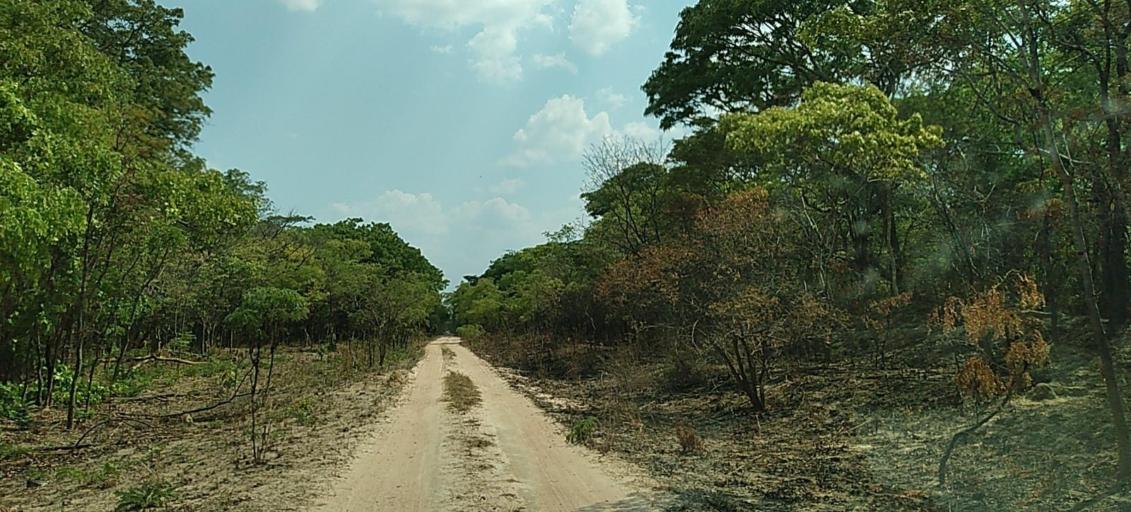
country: ZM
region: Copperbelt
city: Mpongwe
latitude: -13.8648
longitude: 27.9259
